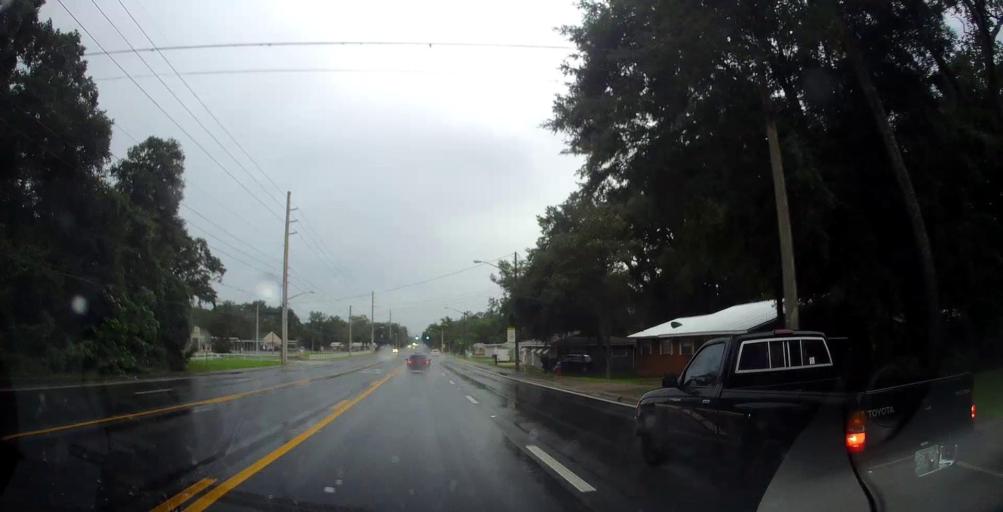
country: US
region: Florida
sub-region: Marion County
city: Ocala
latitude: 29.1828
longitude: -82.0869
